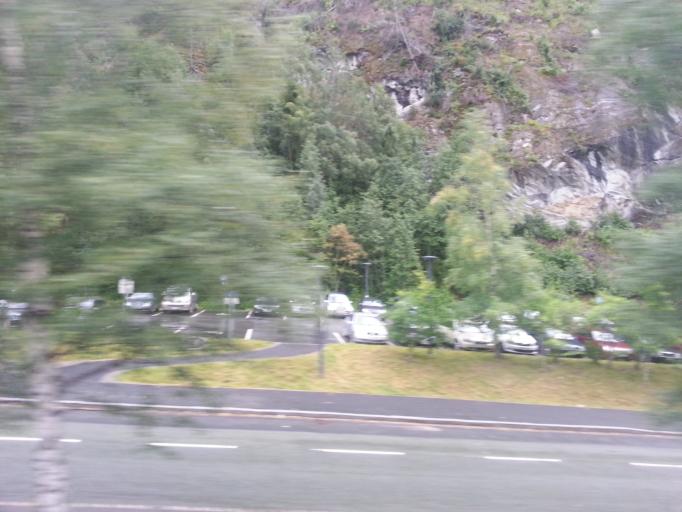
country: NO
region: Sor-Trondelag
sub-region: Malvik
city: Hommelvik
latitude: 63.4130
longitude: 10.8208
